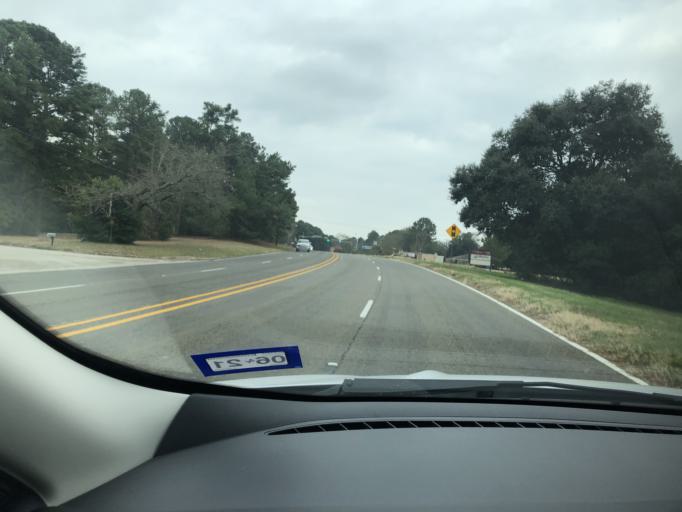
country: US
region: Texas
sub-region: Nacogdoches County
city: Nacogdoches
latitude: 31.6320
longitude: -94.6302
